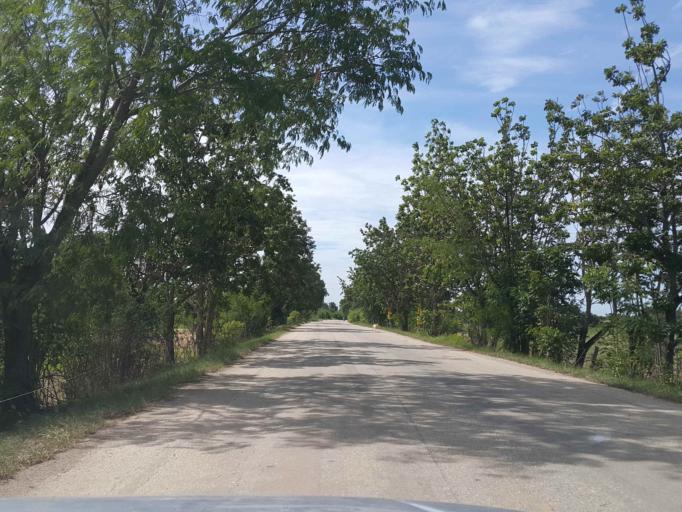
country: TH
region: Sukhothai
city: Ban Dan Lan Hoi
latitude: 17.1460
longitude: 99.5223
